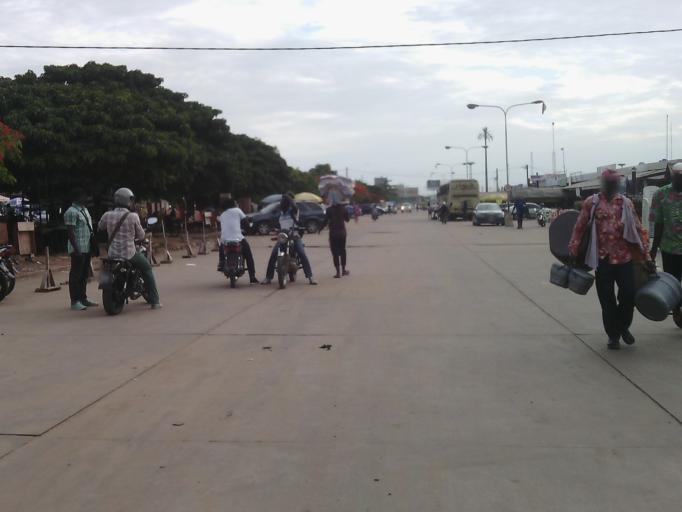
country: BJ
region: Littoral
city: Cotonou
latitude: 6.3852
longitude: 2.3821
